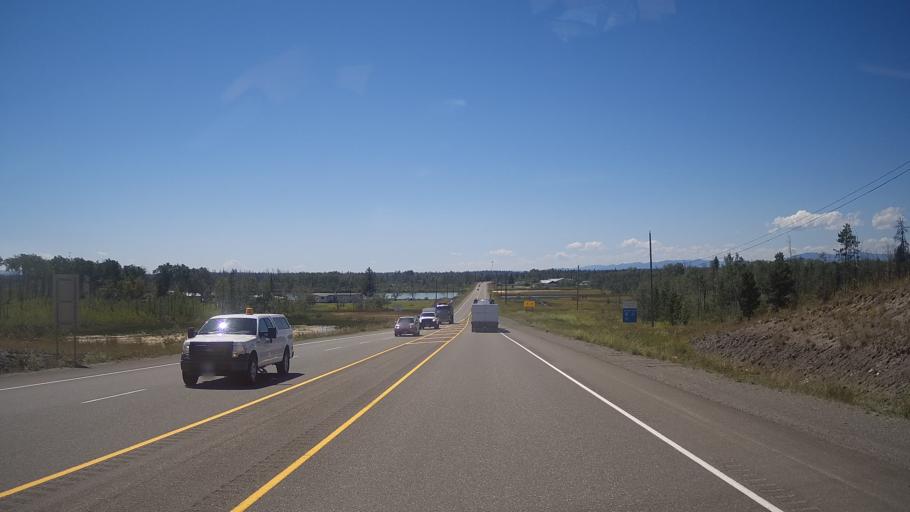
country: CA
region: British Columbia
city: Cache Creek
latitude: 51.3243
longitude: -121.3867
